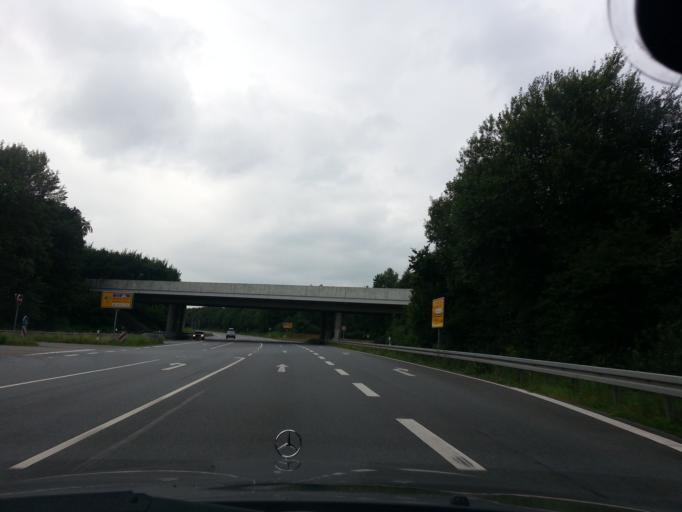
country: DE
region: North Rhine-Westphalia
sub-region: Regierungsbezirk Munster
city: Borken
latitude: 51.8291
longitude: 6.8498
